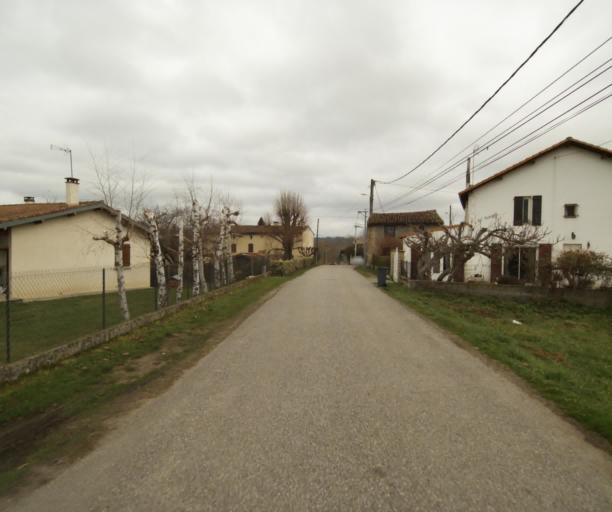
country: FR
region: Midi-Pyrenees
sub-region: Departement de l'Ariege
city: Pamiers
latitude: 43.1361
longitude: 1.6015
